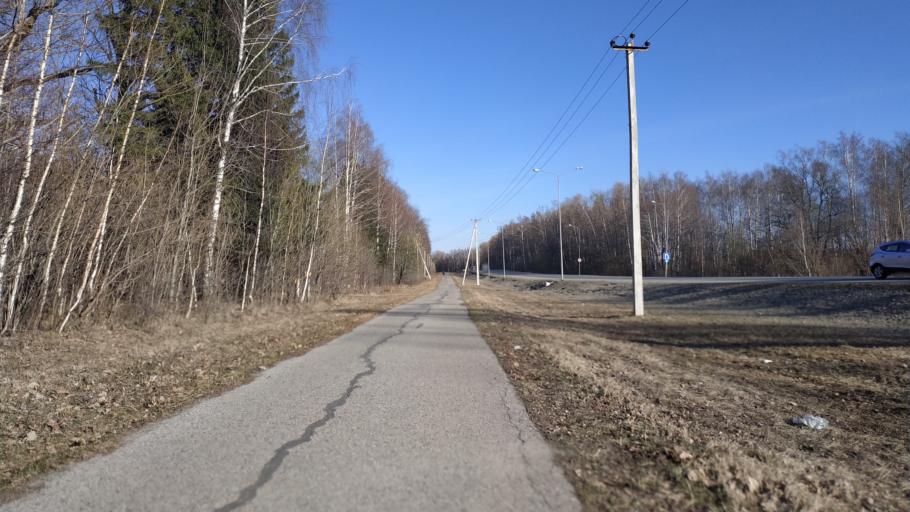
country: RU
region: Chuvashia
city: Novyye Lapsary
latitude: 56.1316
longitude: 47.1122
